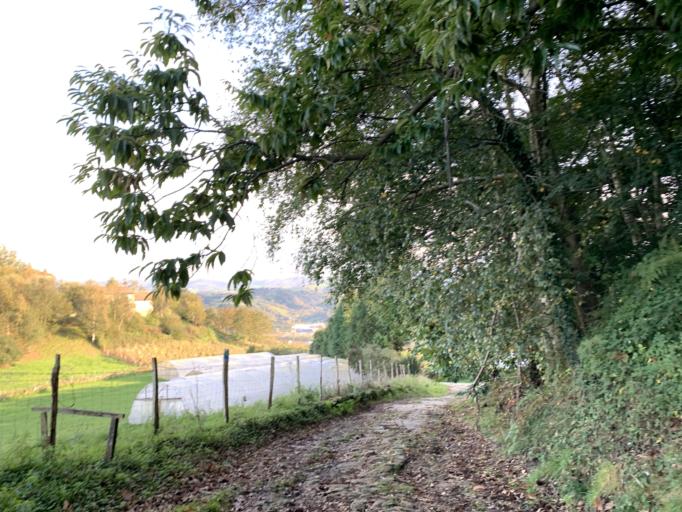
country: ES
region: Basque Country
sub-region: Provincia de Guipuzcoa
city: Zarautz
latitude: 43.2898
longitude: -2.1833
